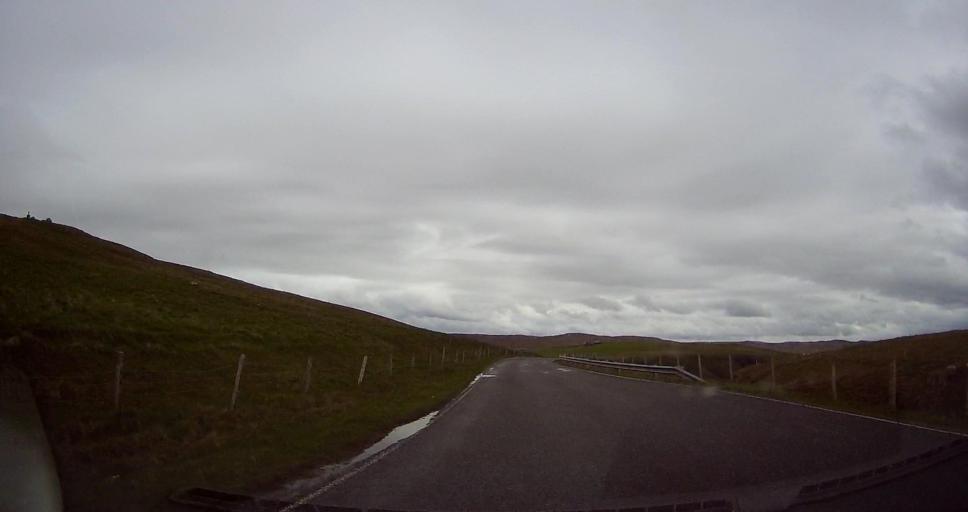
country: GB
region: Scotland
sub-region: Shetland Islands
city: Lerwick
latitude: 60.4860
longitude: -1.5074
